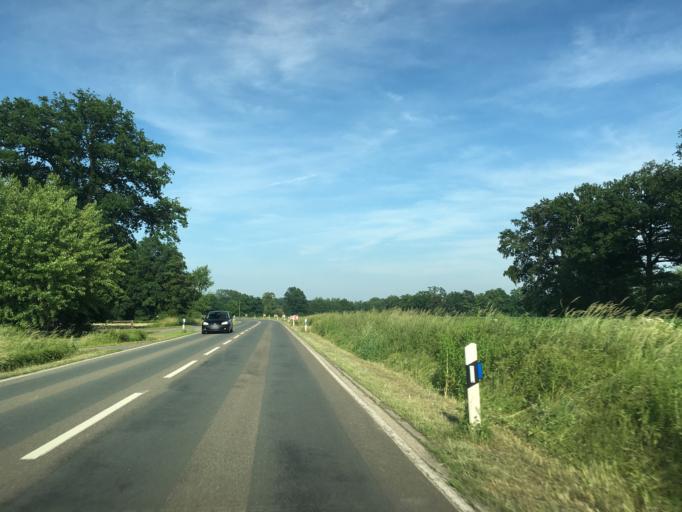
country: DE
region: North Rhine-Westphalia
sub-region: Regierungsbezirk Munster
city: Nordwalde
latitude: 52.0831
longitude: 7.5268
